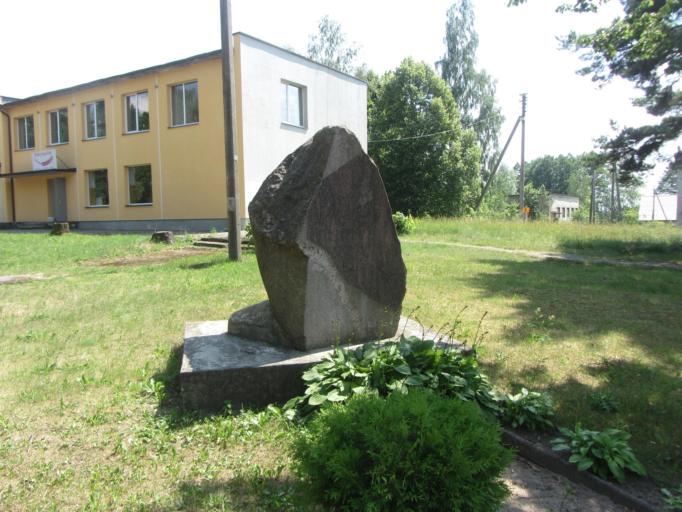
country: LT
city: Lazdijai
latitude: 54.2949
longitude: 23.5515
